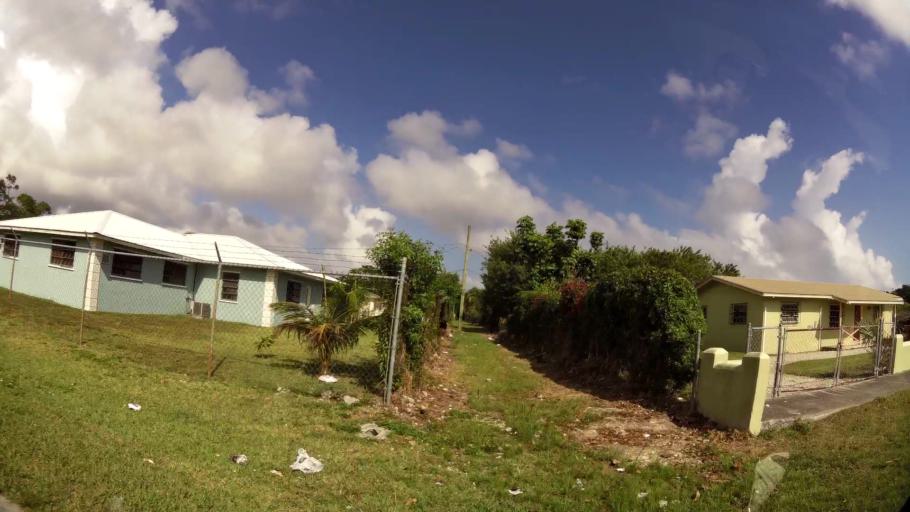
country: BS
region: Freeport
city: Lucaya
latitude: 26.5297
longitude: -78.6809
